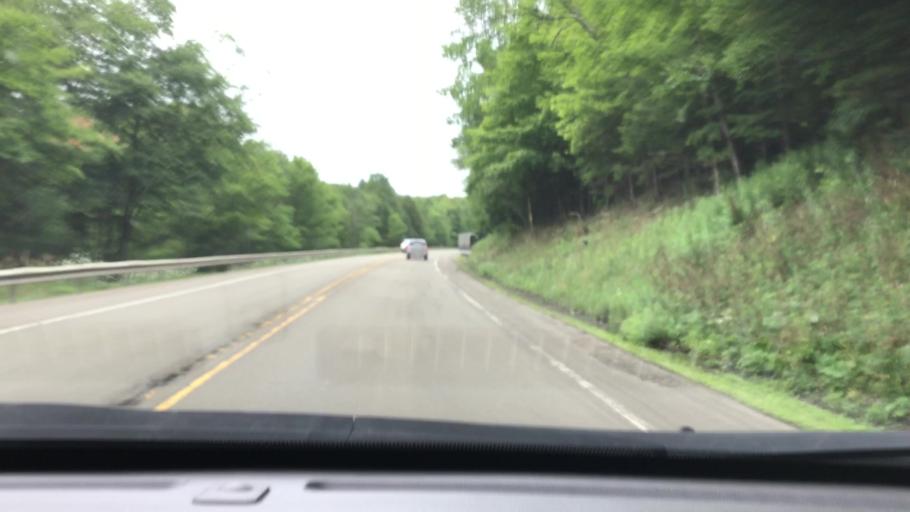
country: US
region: Pennsylvania
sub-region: McKean County
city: Kane
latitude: 41.6647
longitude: -78.6816
